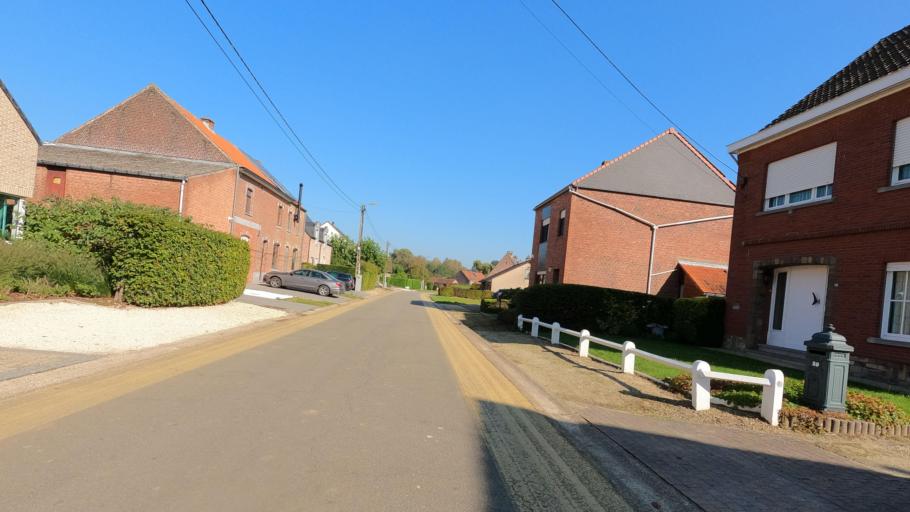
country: BE
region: Flanders
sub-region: Provincie Vlaams-Brabant
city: Rotselaar
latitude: 50.9464
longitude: 4.7301
